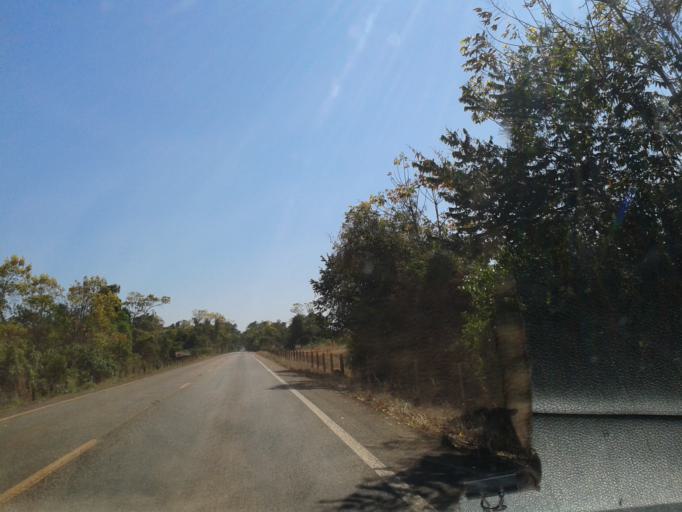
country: BR
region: Goias
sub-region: Crixas
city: Crixas
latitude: -14.0288
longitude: -50.3277
